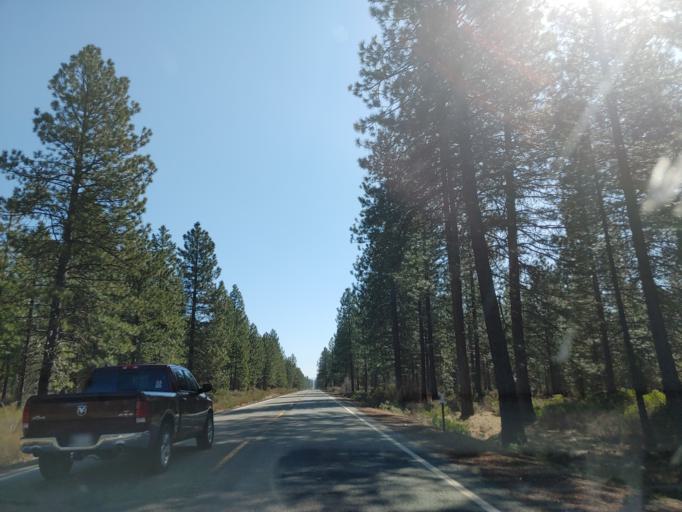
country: US
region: California
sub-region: Siskiyou County
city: McCloud
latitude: 41.2524
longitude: -122.1051
